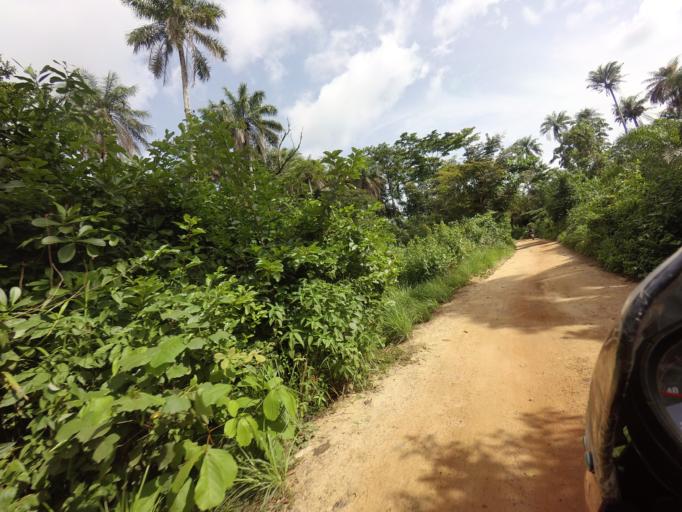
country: SL
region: Eastern Province
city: Jojoima
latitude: 7.8613
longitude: -10.8008
